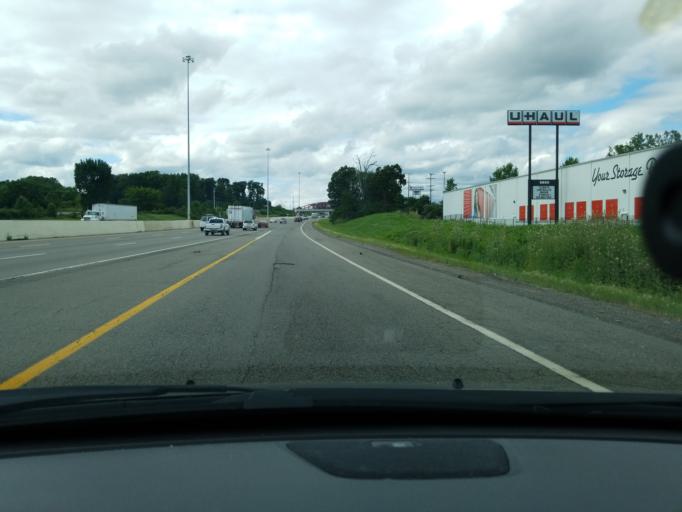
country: US
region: Ohio
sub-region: Stark County
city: North Canton
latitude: 40.8646
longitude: -81.4284
